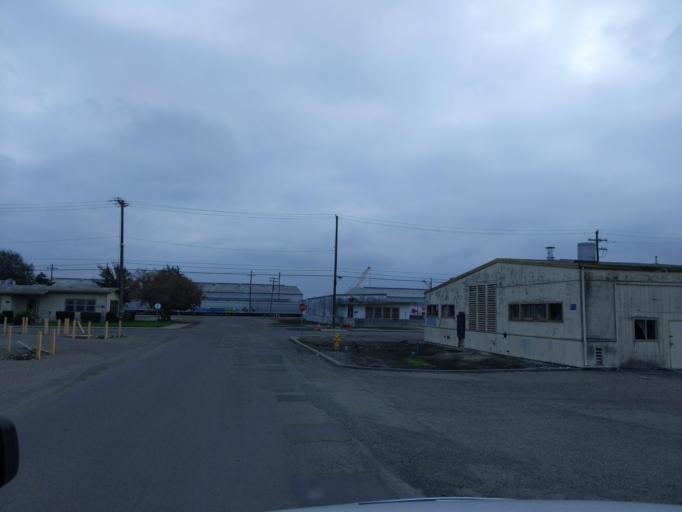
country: US
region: California
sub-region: San Joaquin County
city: Country Club
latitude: 37.9503
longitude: -121.3636
